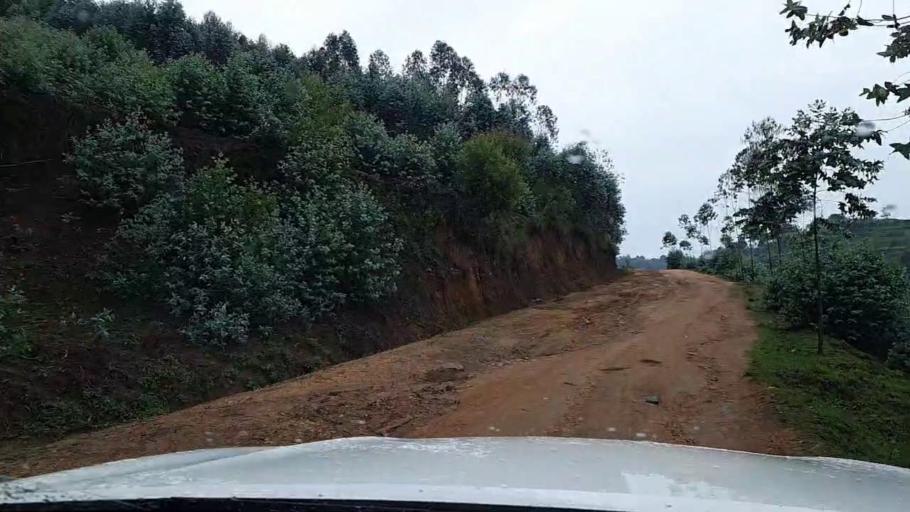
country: RW
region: Southern Province
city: Nzega
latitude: -2.4691
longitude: 29.5031
